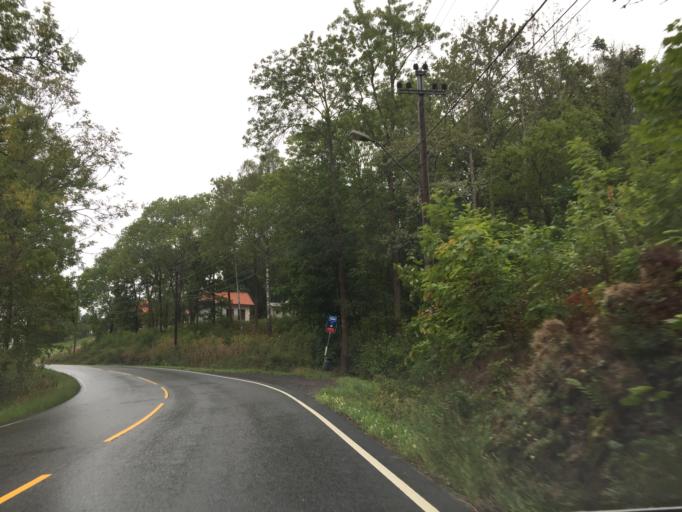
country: NO
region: Akershus
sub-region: Baerum
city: Lysaker
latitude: 59.9777
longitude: 10.6232
